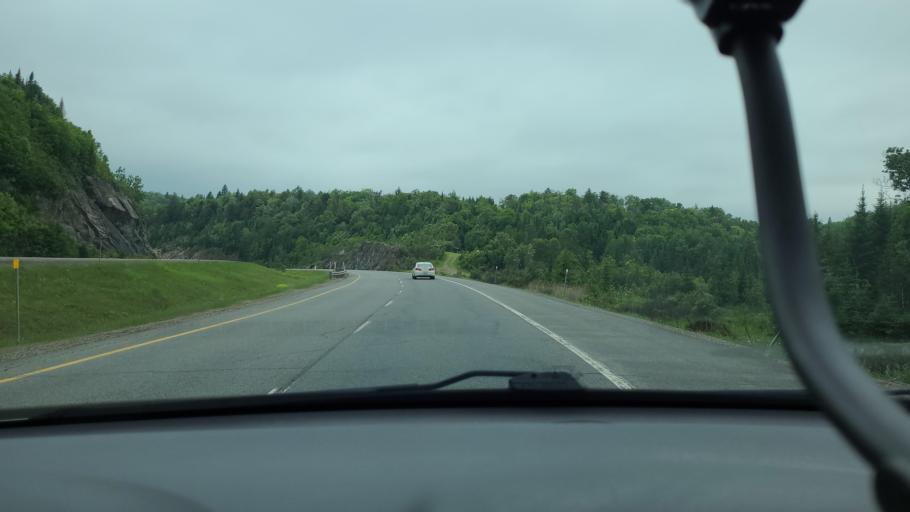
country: CA
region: Quebec
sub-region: Laurentides
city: Mont-Tremblant
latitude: 46.1539
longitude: -74.6636
